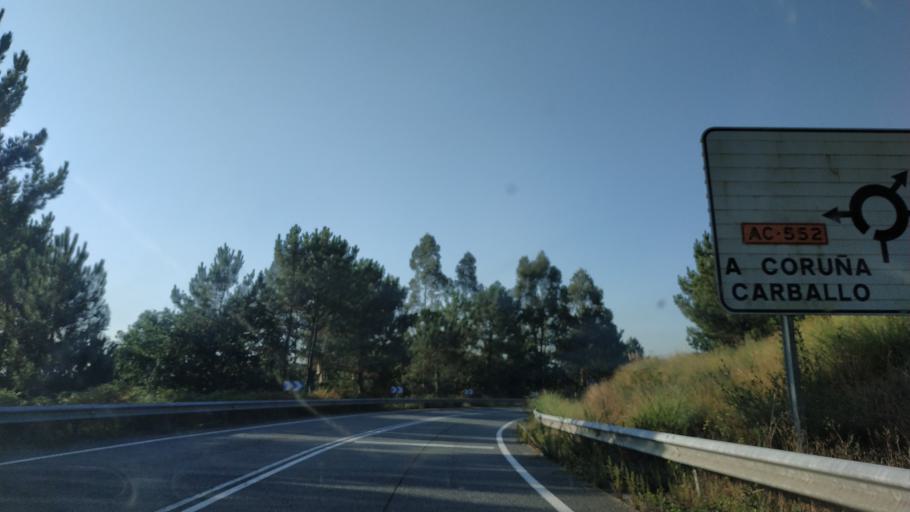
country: ES
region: Galicia
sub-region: Provincia da Coruna
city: Carballo
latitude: 43.2334
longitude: -8.6782
